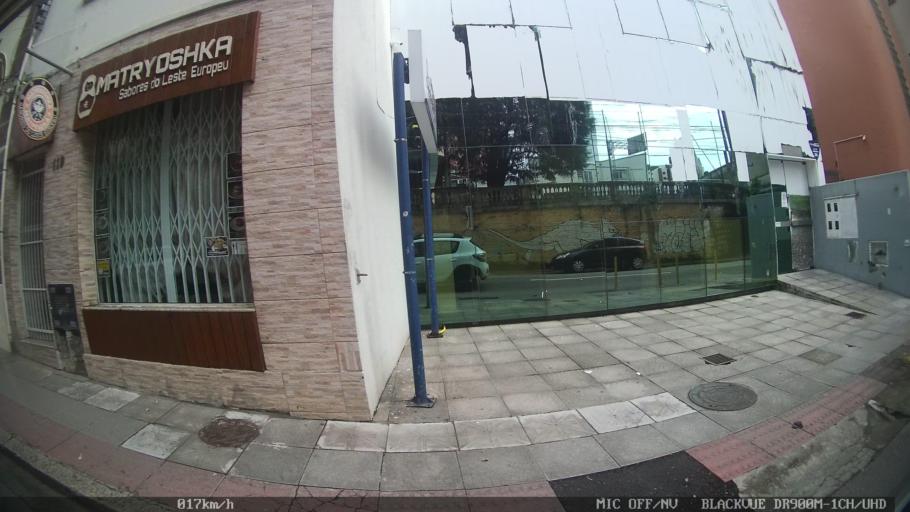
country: BR
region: Santa Catarina
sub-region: Florianopolis
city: Florianopolis
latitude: -27.5951
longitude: -48.5499
